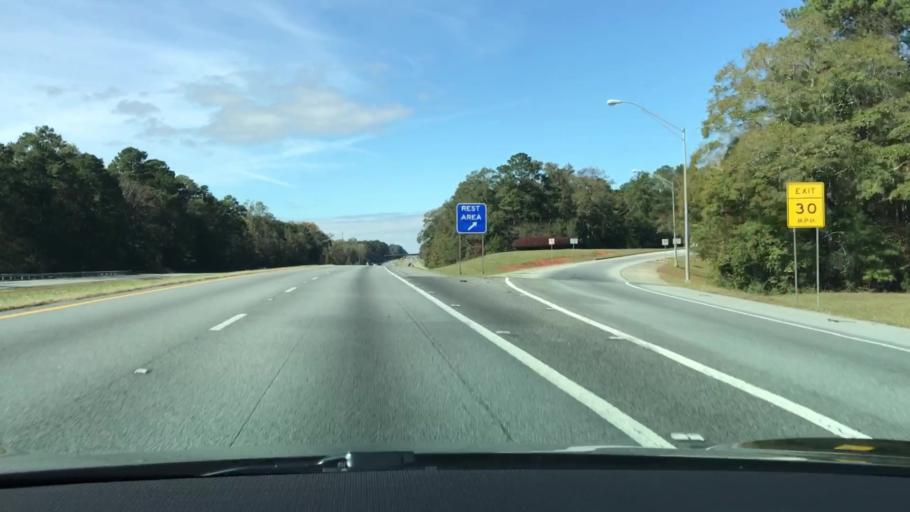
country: US
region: Georgia
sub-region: Morgan County
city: Madison
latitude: 33.5776
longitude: -83.5745
